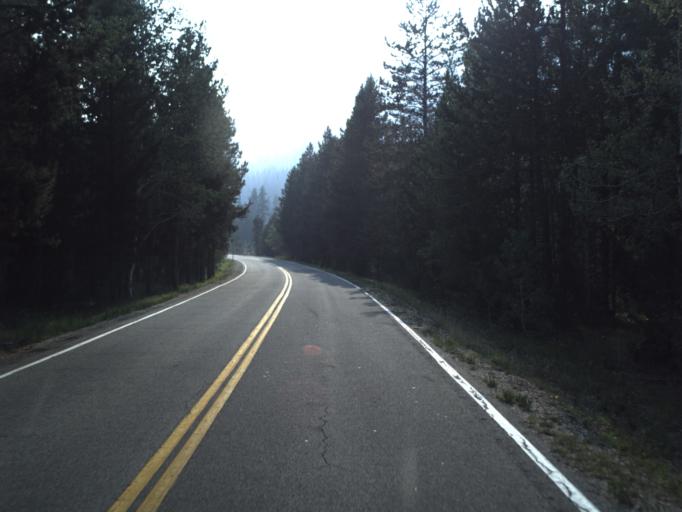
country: US
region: Utah
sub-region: Summit County
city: Francis
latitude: 40.5929
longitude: -111.0106
